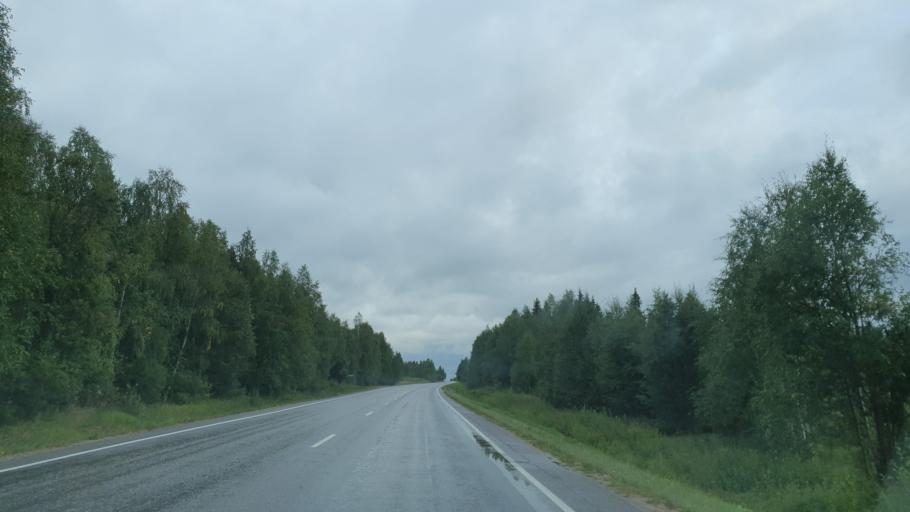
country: FI
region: Lapland
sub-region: Tunturi-Lappi
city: Kolari
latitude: 67.2339
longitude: 23.8892
